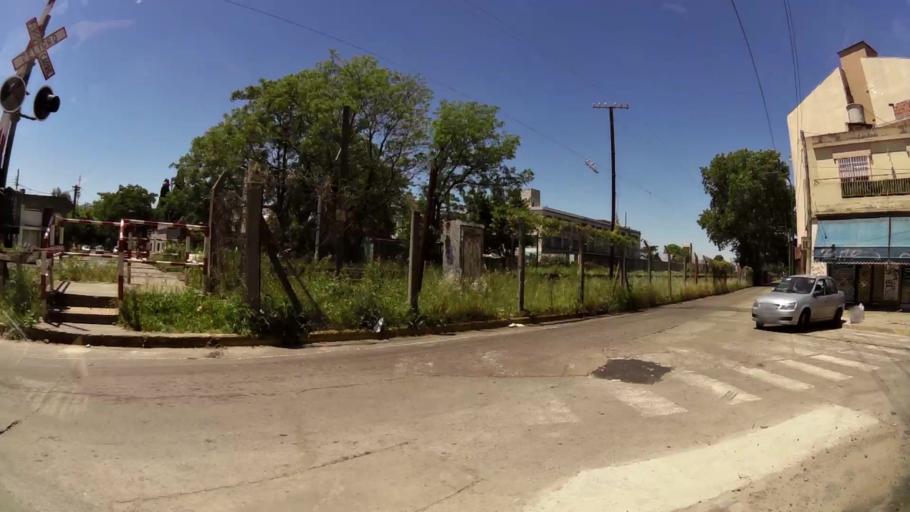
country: AR
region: Buenos Aires
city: Caseros
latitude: -34.5932
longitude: -58.5513
